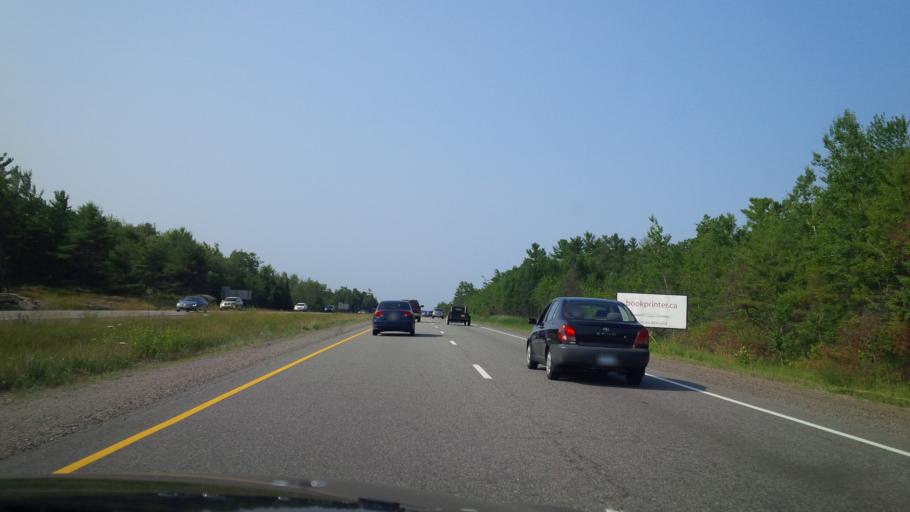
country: CA
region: Ontario
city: Bracebridge
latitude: 44.9716
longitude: -79.3200
